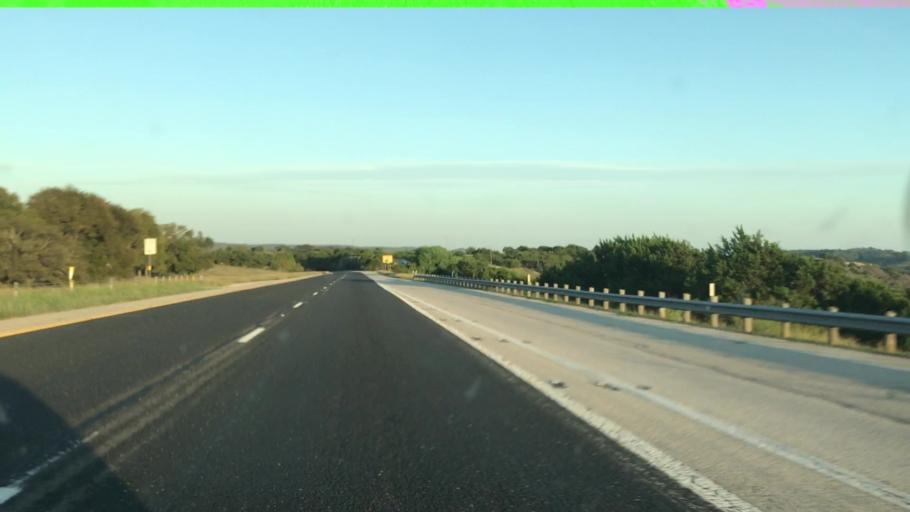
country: US
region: Texas
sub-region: Kerr County
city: Kerrville
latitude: 30.0533
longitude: -99.0252
